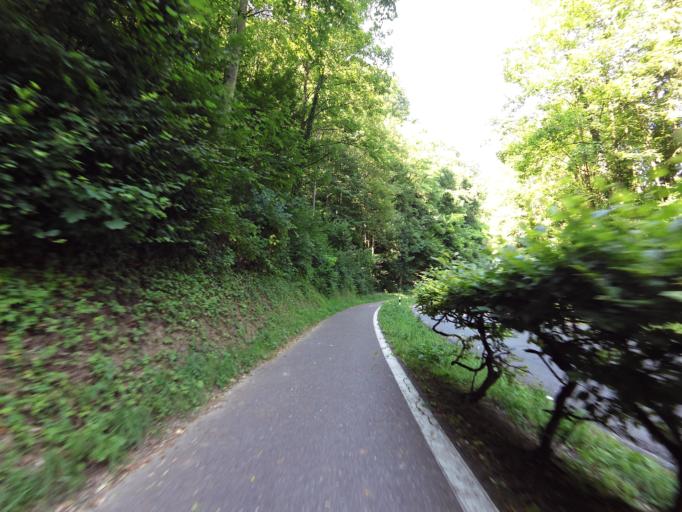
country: CH
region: Aargau
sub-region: Bezirk Brugg
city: Hausen
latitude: 47.4619
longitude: 8.2259
